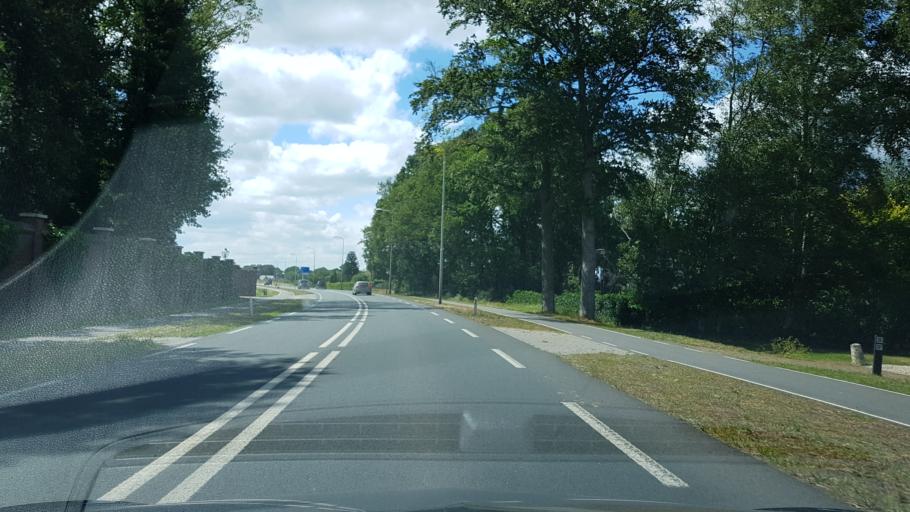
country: NL
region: Gelderland
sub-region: Gemeente Putten
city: Putten
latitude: 52.2559
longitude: 5.5792
